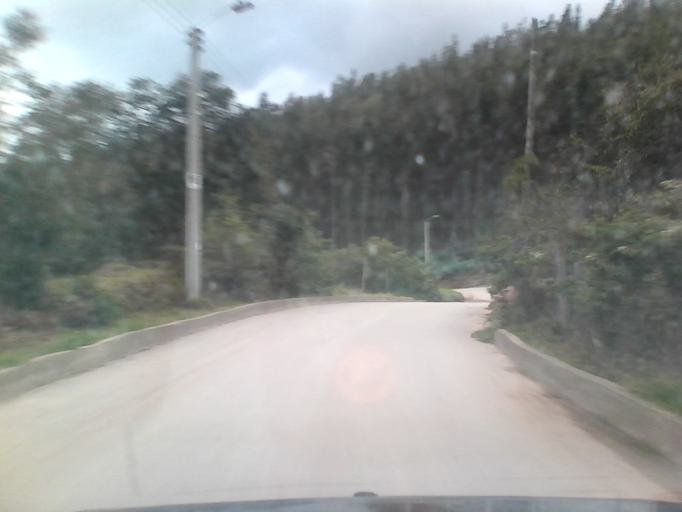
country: CO
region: Boyaca
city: Duitama
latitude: 5.8477
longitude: -73.0372
